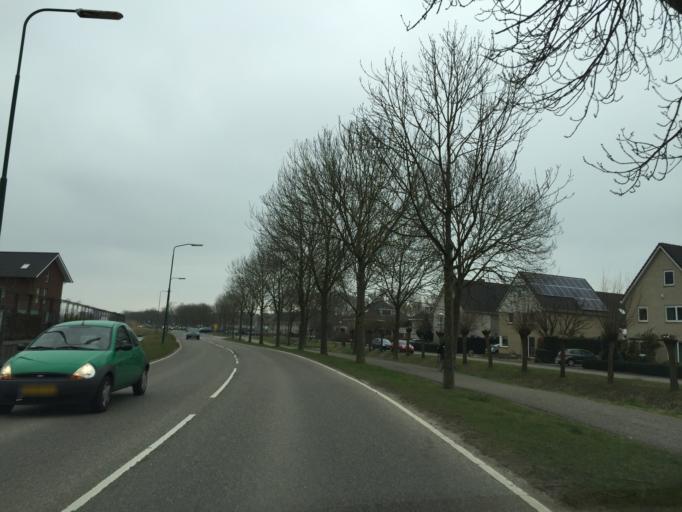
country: NL
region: Utrecht
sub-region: Stichtse Vecht
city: Spechtenkamp
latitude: 52.0891
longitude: 5.0257
